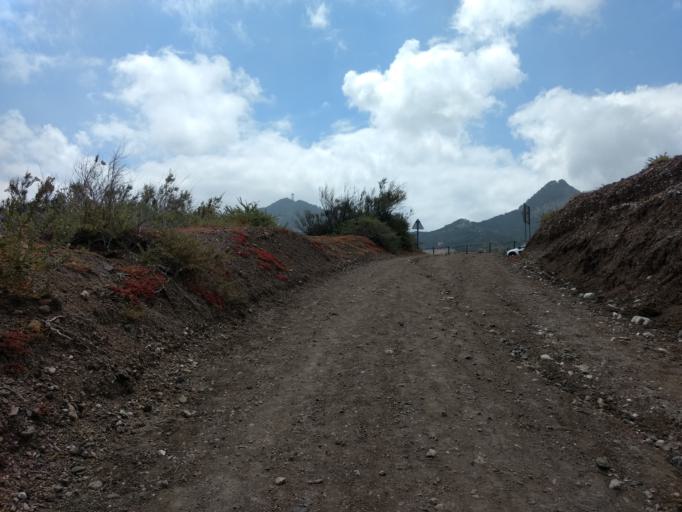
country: PT
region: Madeira
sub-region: Porto Santo
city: Camacha
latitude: 33.0917
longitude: -16.3442
